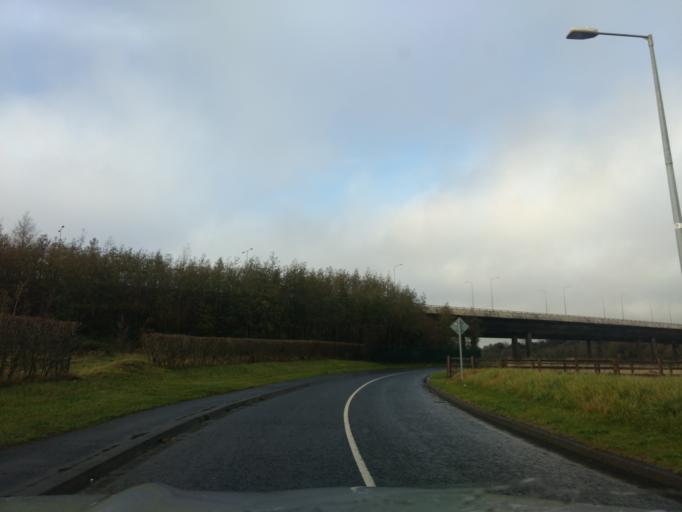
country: IE
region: Leinster
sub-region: Fingal County
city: Swords
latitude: 53.4636
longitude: -6.2022
